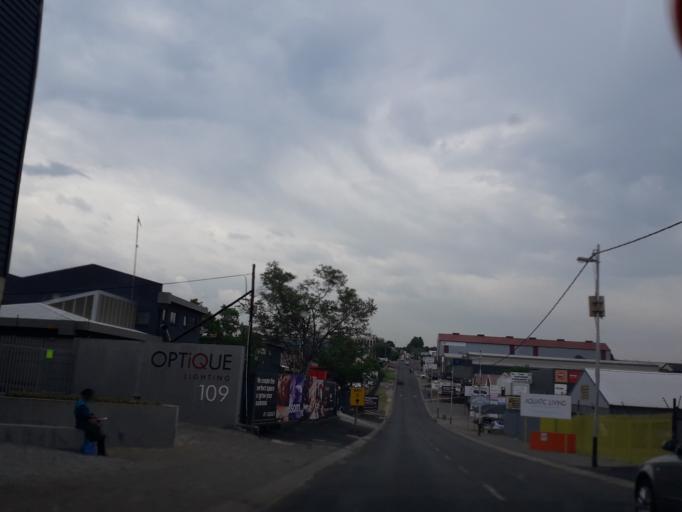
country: ZA
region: Gauteng
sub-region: City of Johannesburg Metropolitan Municipality
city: Modderfontein
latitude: -26.1048
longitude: 28.0818
